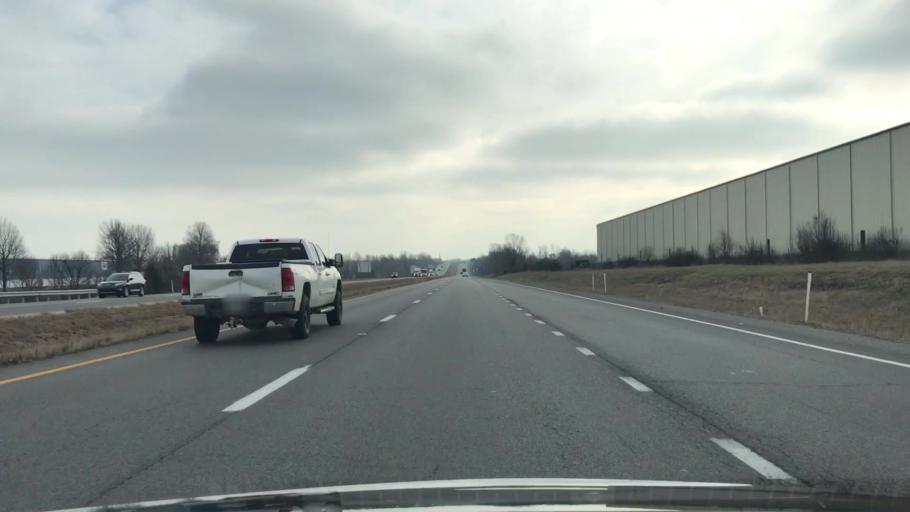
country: US
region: Kentucky
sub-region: Hopkins County
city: Madisonville
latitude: 37.3499
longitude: -87.4851
